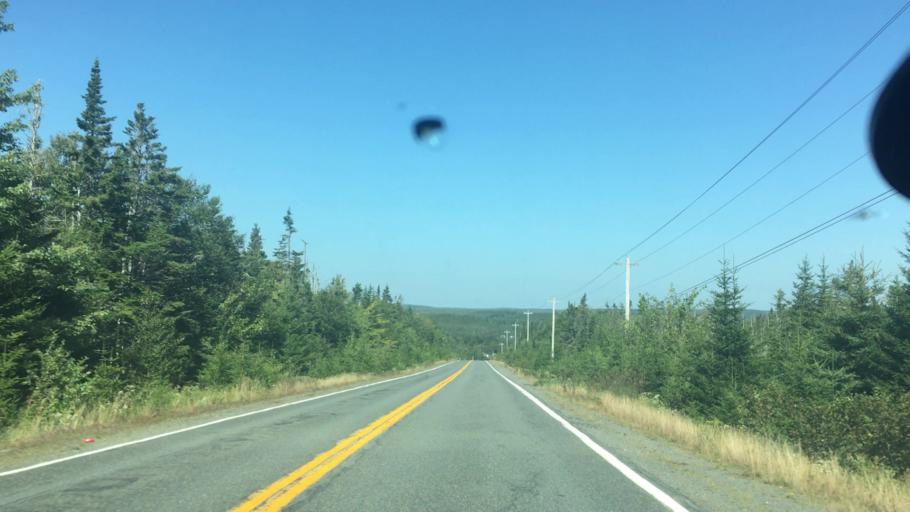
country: CA
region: Nova Scotia
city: Antigonish
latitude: 44.9924
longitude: -62.0970
